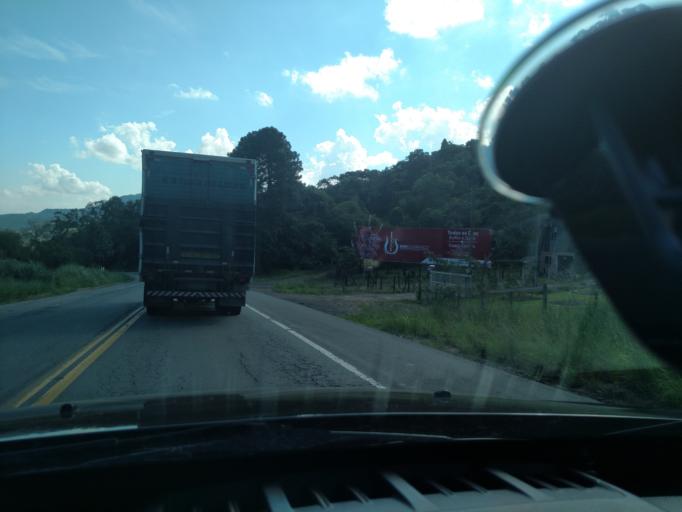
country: BR
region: Santa Catarina
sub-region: Ibirama
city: Ibirama
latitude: -27.1145
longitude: -49.5310
